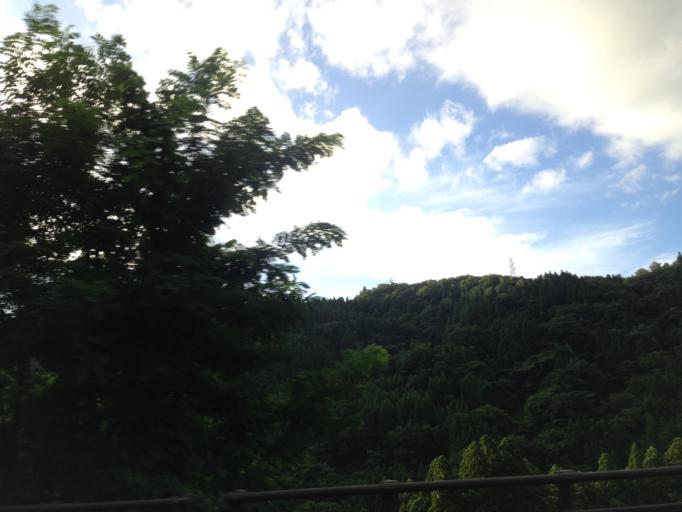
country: JP
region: Toyama
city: Nanto-shi
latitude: 36.5638
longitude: 137.0029
